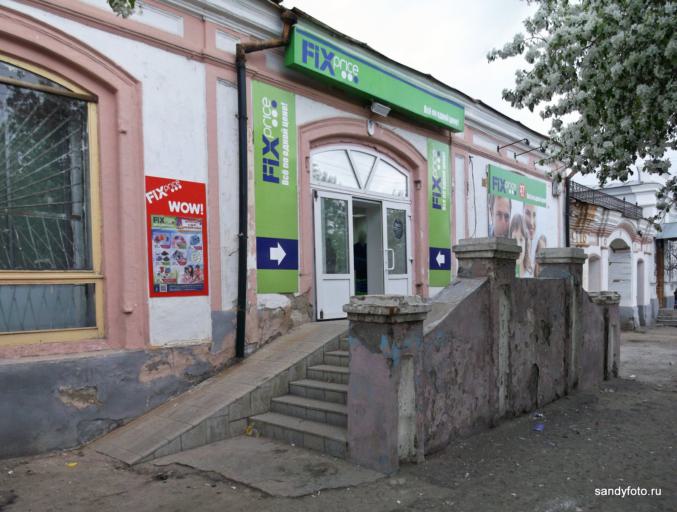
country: RU
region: Chelyabinsk
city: Troitsk
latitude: 54.0822
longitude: 61.5583
